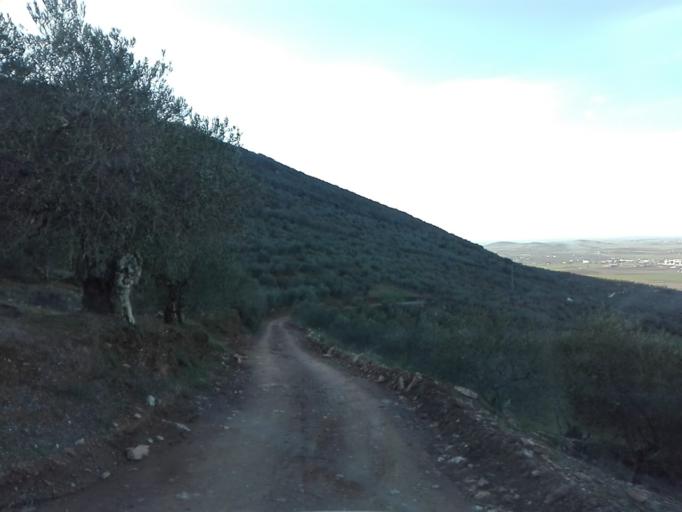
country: ES
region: Extremadura
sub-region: Provincia de Badajoz
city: Llerena
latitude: 38.2146
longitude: -5.9984
